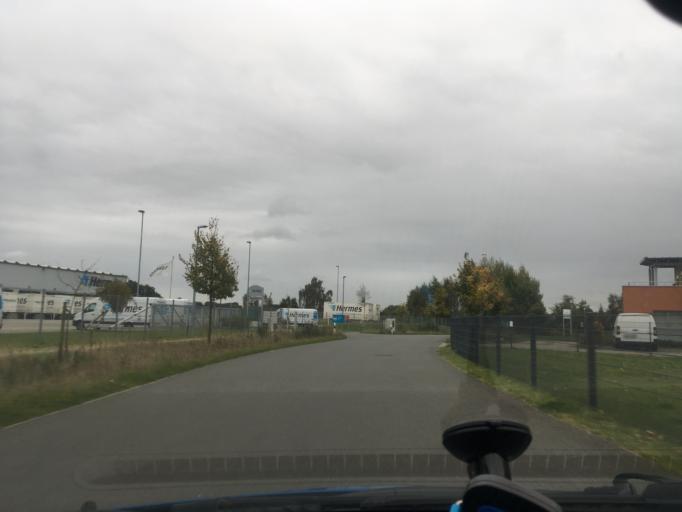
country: DE
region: Lower Saxony
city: Wittorf
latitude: 53.3116
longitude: 10.3703
